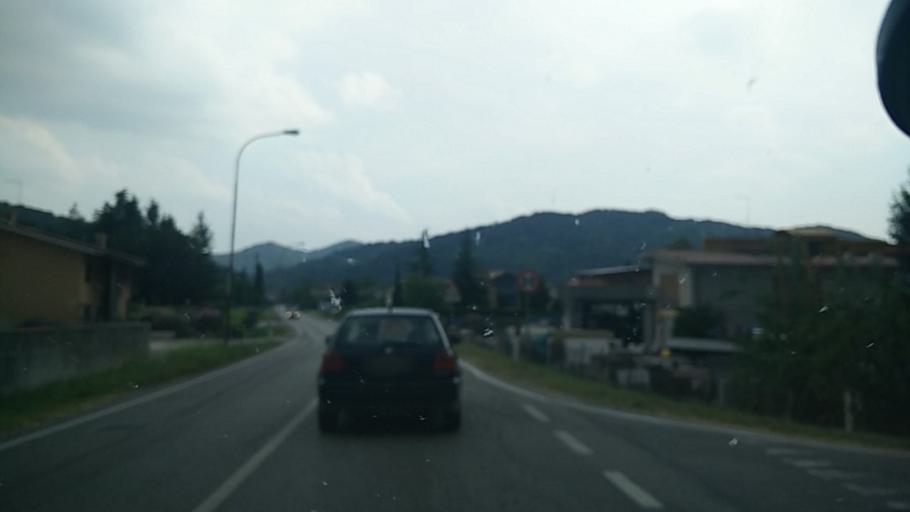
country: IT
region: Veneto
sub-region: Provincia di Treviso
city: Follina
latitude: 45.9576
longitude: 12.1233
